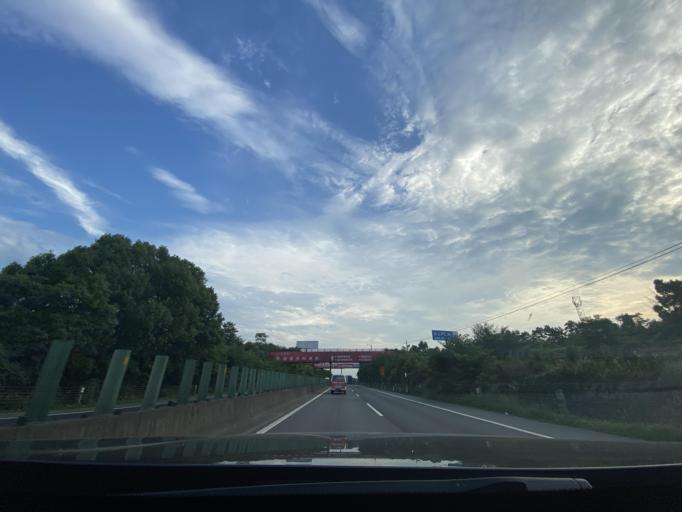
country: CN
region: Sichuan
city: Luojiang
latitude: 31.4072
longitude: 104.5753
